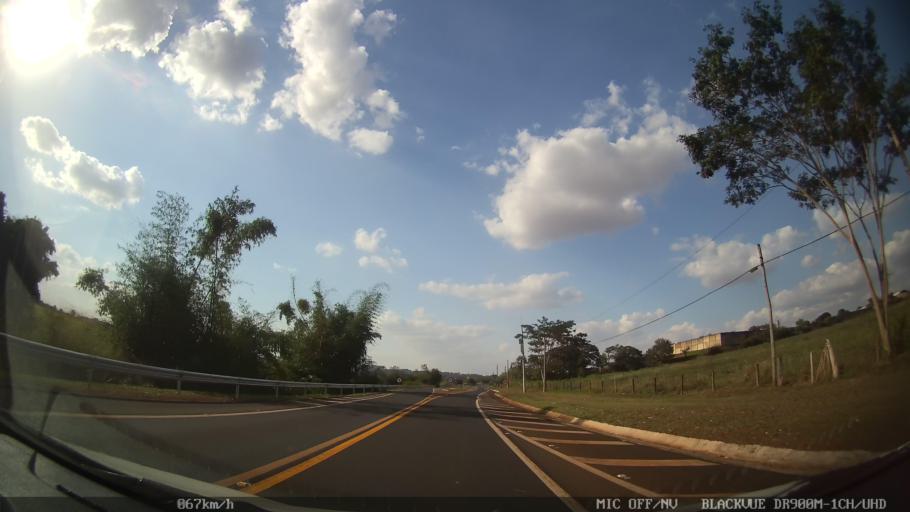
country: BR
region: Sao Paulo
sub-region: Ribeirao Preto
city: Ribeirao Preto
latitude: -21.1901
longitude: -47.8657
